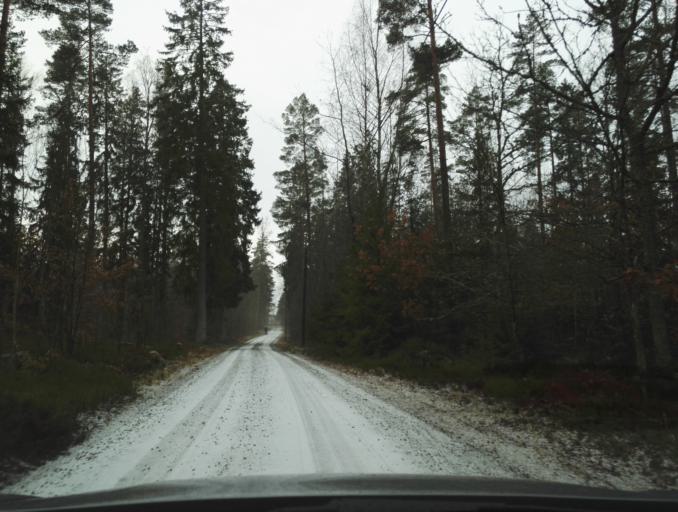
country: SE
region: Kronoberg
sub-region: Vaxjo Kommun
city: Vaexjoe
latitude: 56.9189
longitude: 14.7490
